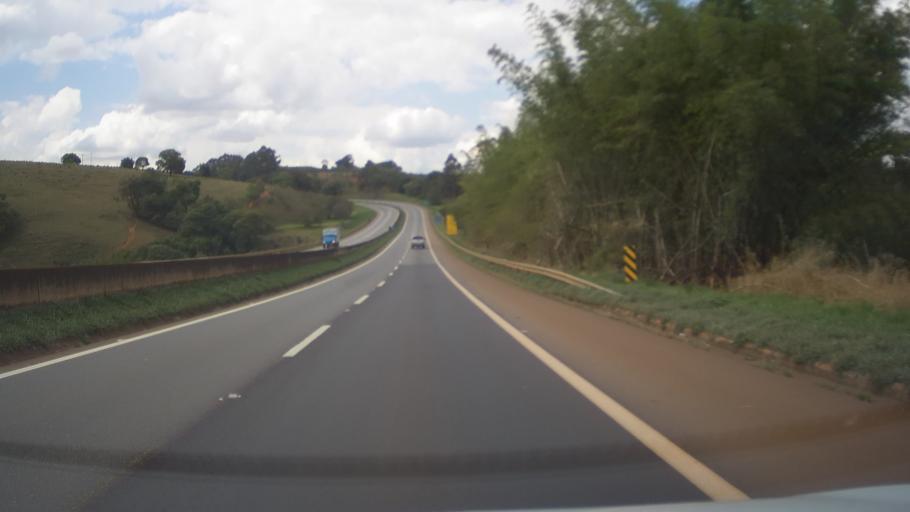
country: BR
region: Minas Gerais
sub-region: Nepomuceno
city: Nepomuceno
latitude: -21.2758
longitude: -45.1385
